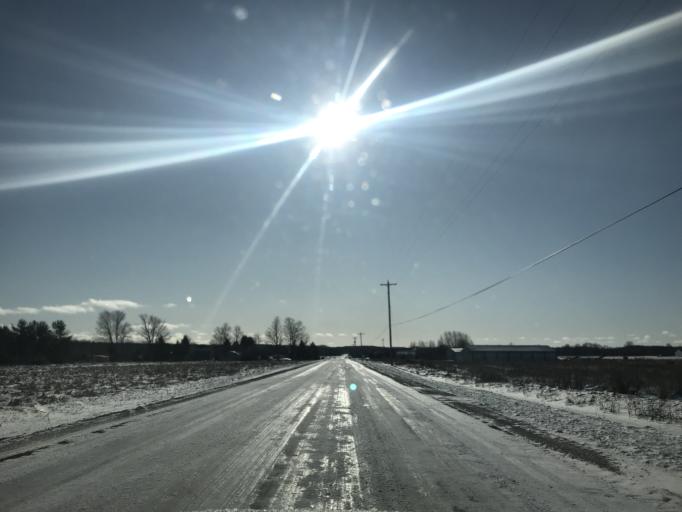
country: US
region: Wisconsin
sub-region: Door County
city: Sturgeon Bay
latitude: 44.8401
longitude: -87.5040
